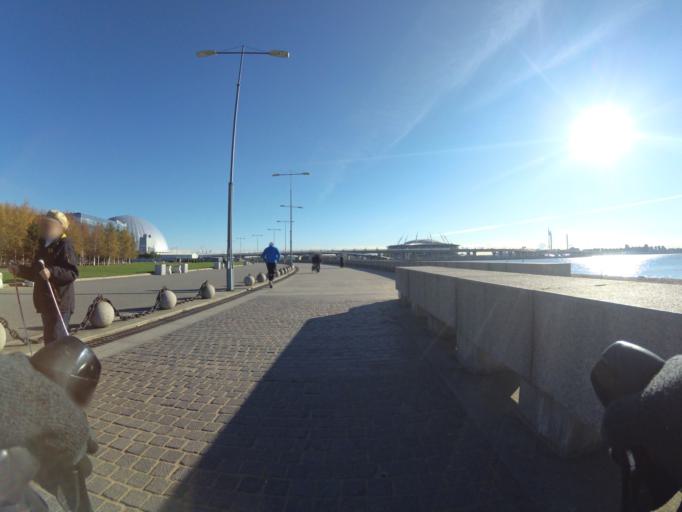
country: RU
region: Leningrad
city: Untolovo
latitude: 59.9800
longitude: 30.2044
